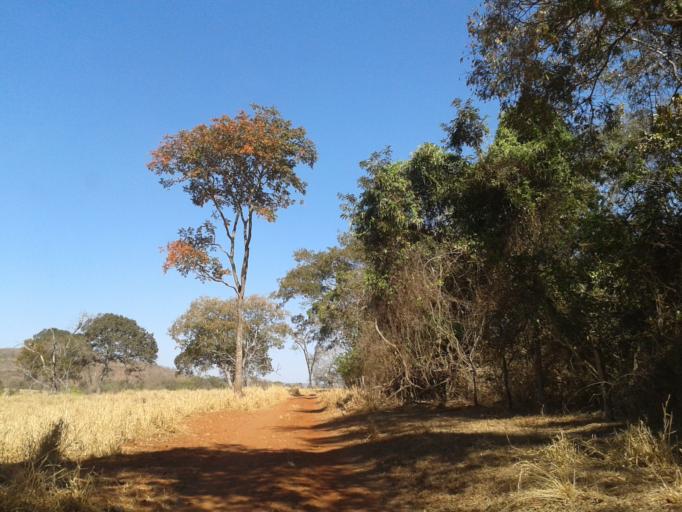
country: BR
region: Minas Gerais
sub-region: Santa Vitoria
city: Santa Vitoria
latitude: -19.1348
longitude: -50.0398
